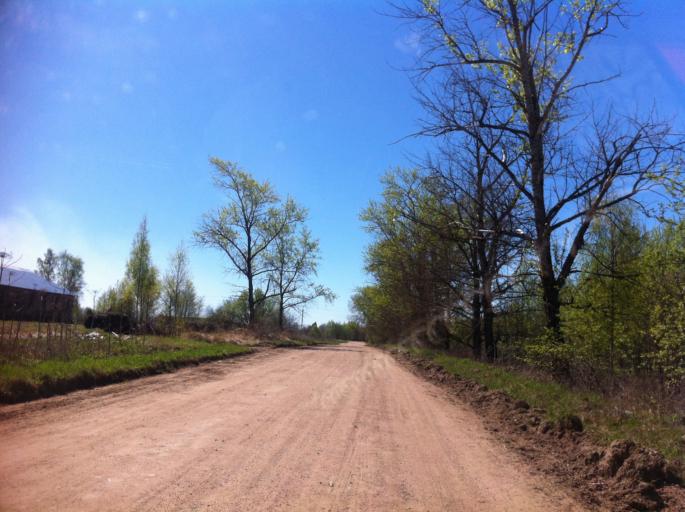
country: RU
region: Pskov
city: Izborsk
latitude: 57.7905
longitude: 27.9631
